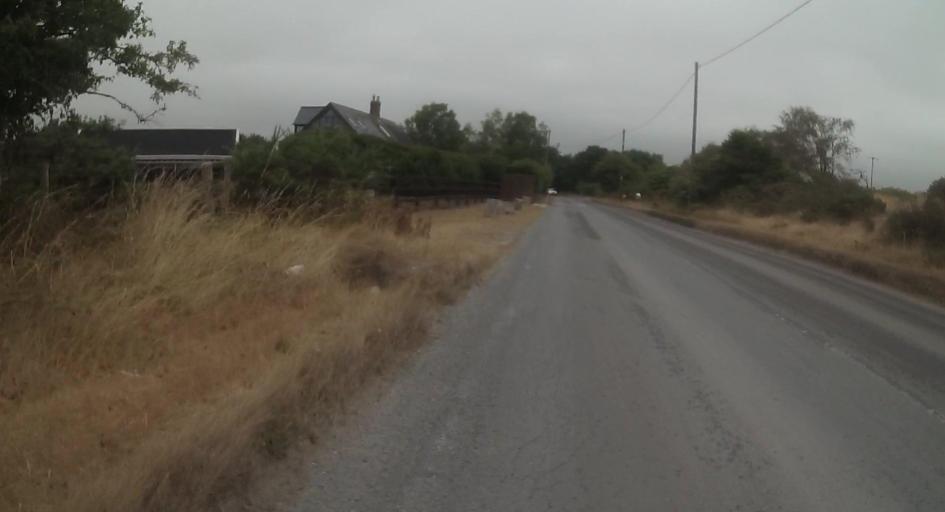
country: GB
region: England
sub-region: Dorset
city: Wareham
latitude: 50.6619
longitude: -2.1008
